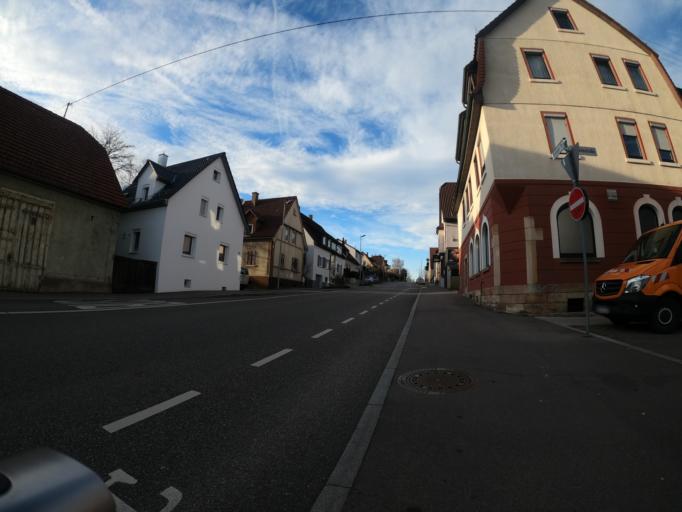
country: DE
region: Baden-Wuerttemberg
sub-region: Regierungsbezirk Stuttgart
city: Denkendorf
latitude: 48.6981
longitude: 9.3125
